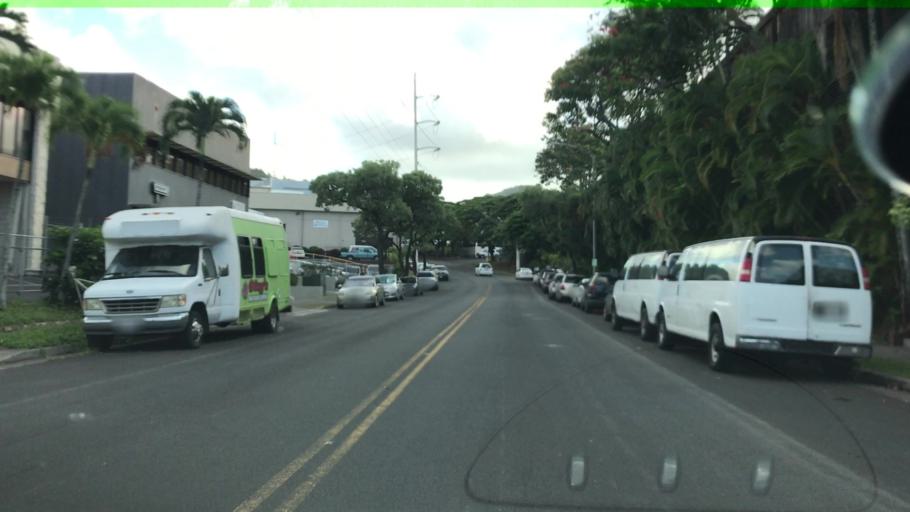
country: US
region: Hawaii
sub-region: Honolulu County
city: Halawa Heights
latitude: 21.3745
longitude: -157.9123
